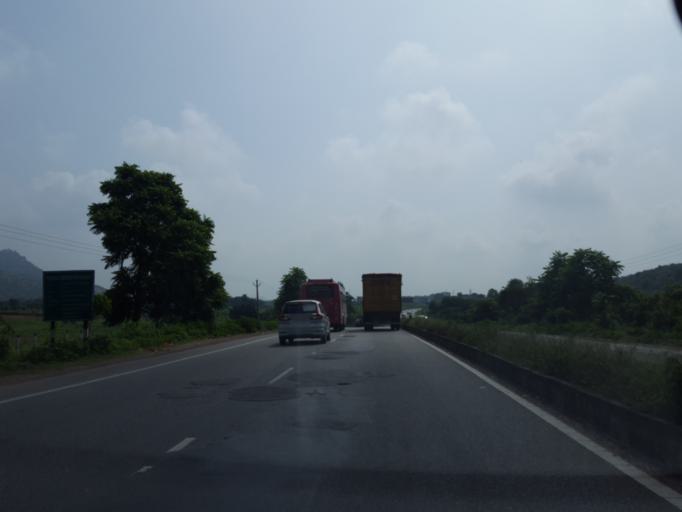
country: IN
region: Telangana
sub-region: Rangareddi
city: Ghatkesar
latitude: 17.2852
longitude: 78.7759
